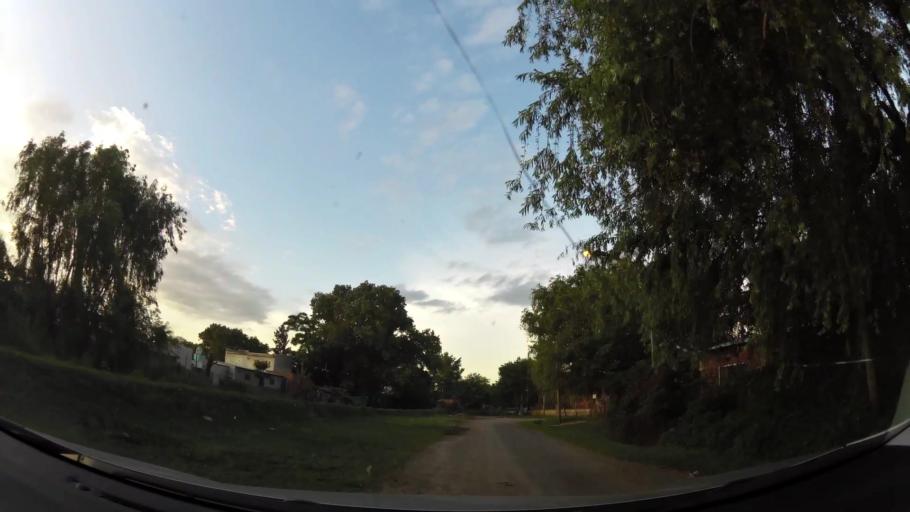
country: AR
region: Buenos Aires
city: Santa Catalina - Dique Lujan
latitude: -34.4469
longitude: -58.6666
